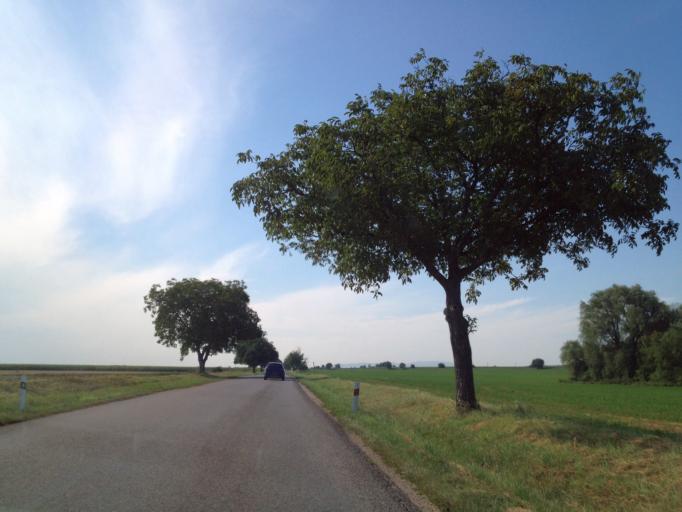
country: SK
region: Nitriansky
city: Svodin
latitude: 47.8926
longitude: 18.4129
